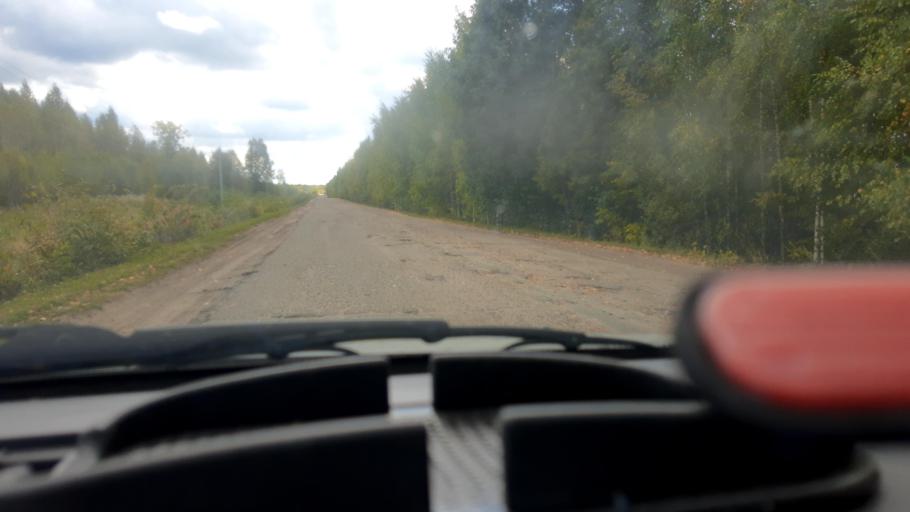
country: RU
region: Mariy-El
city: Kilemary
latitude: 56.8918
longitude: 46.7547
